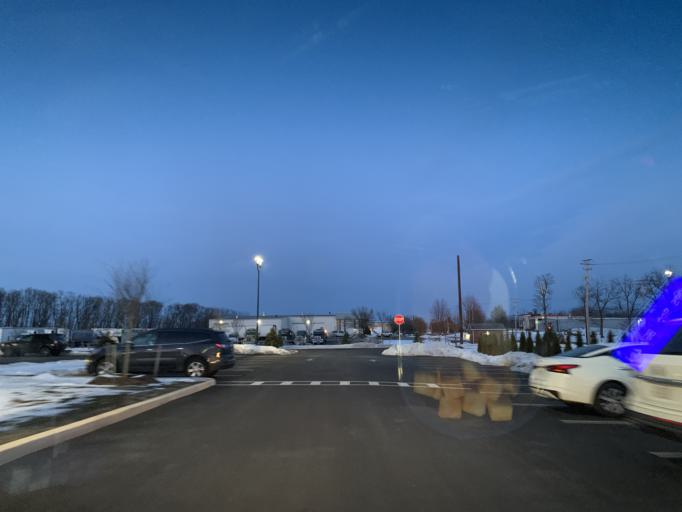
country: US
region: Pennsylvania
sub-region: Cumberland County
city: Carlisle
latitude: 40.1837
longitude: -77.2365
